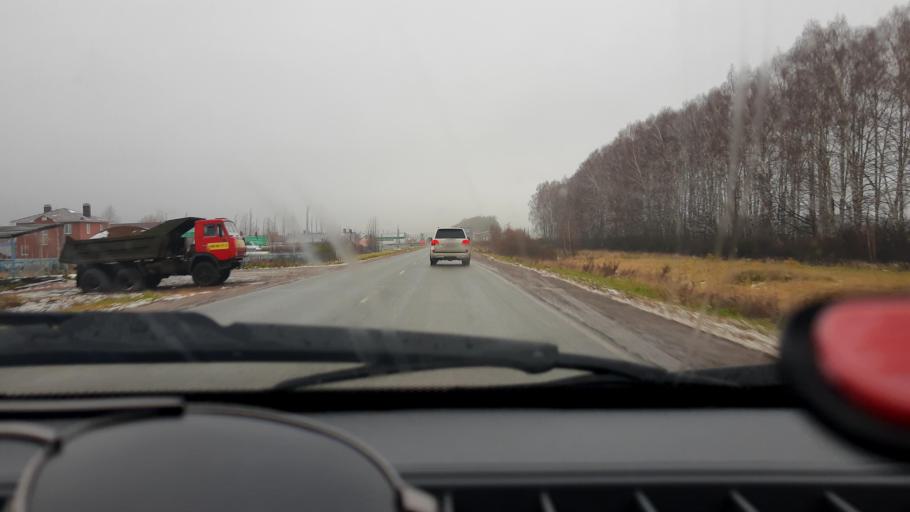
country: RU
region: Bashkortostan
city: Kabakovo
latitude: 54.6047
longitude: 56.1913
